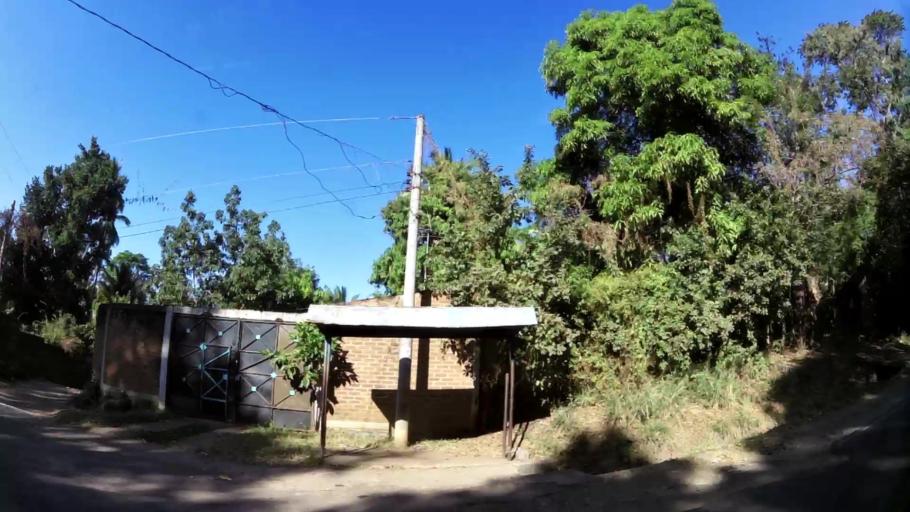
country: SV
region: Sonsonate
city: Sonzacate
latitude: 13.7462
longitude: -89.7082
